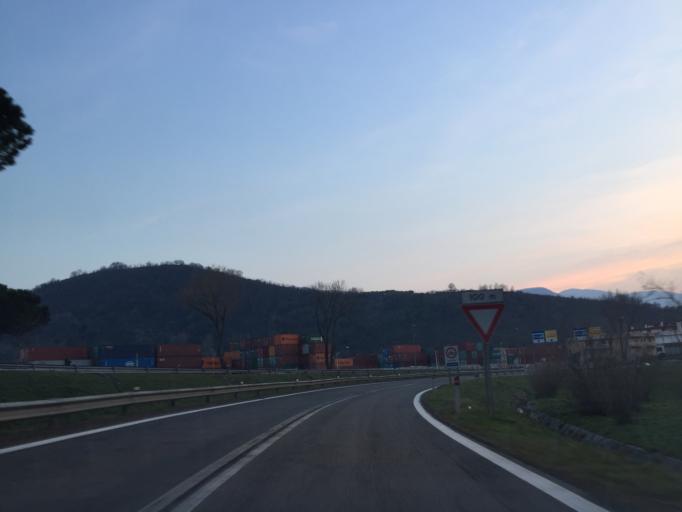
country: IT
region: Campania
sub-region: Provincia di Salerno
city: Lanzara
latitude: 40.7709
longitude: 14.6665
